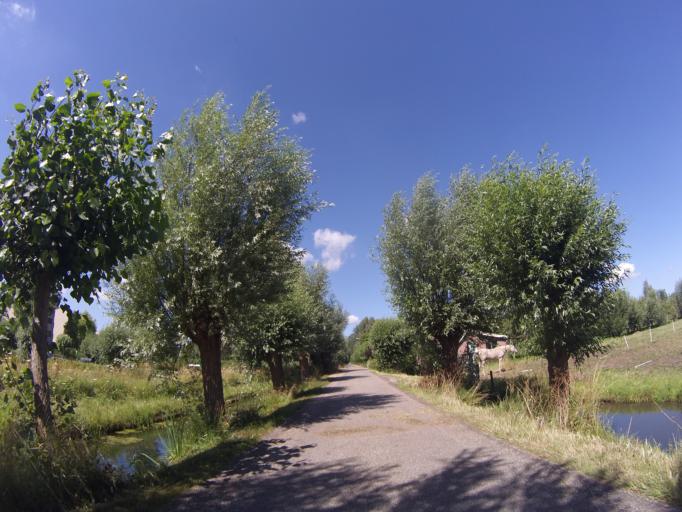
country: NL
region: Utrecht
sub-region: Stichtse Vecht
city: Spechtenkamp
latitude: 52.1118
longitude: 5.0227
